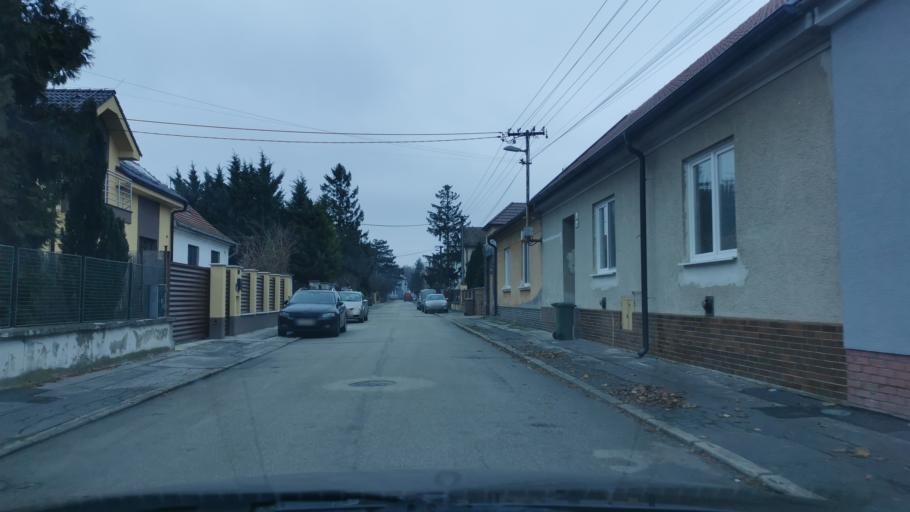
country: SK
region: Trnavsky
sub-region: Okres Skalica
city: Skalica
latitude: 48.8471
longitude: 17.2176
